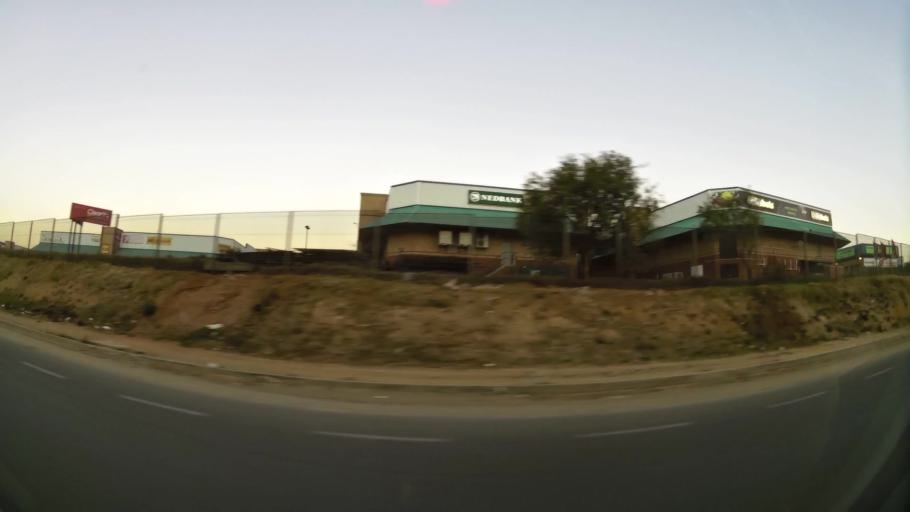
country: ZA
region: Gauteng
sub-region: Ekurhuleni Metropolitan Municipality
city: Tembisa
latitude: -26.0264
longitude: 28.1952
